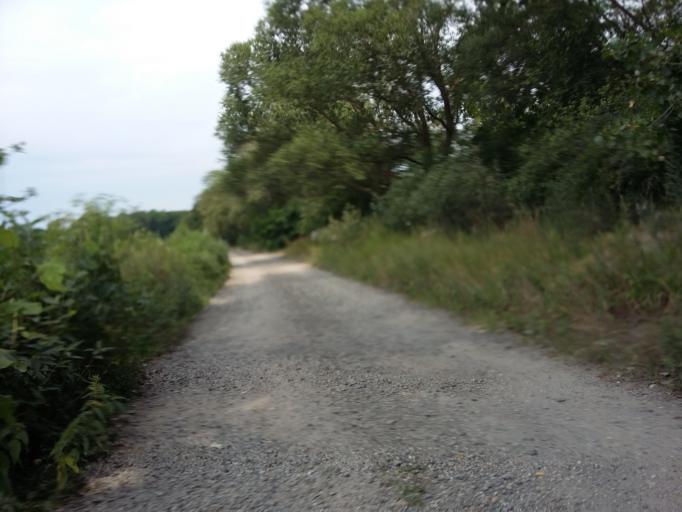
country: AT
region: Lower Austria
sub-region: Politischer Bezirk Ganserndorf
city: Drosing
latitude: 48.4939
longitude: 16.9486
